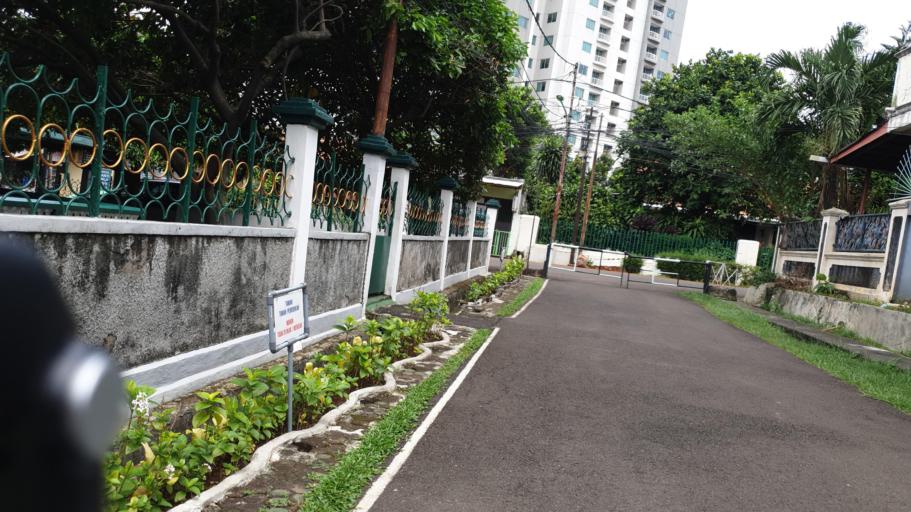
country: ID
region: Banten
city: South Tangerang
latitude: -6.2825
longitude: 106.7950
